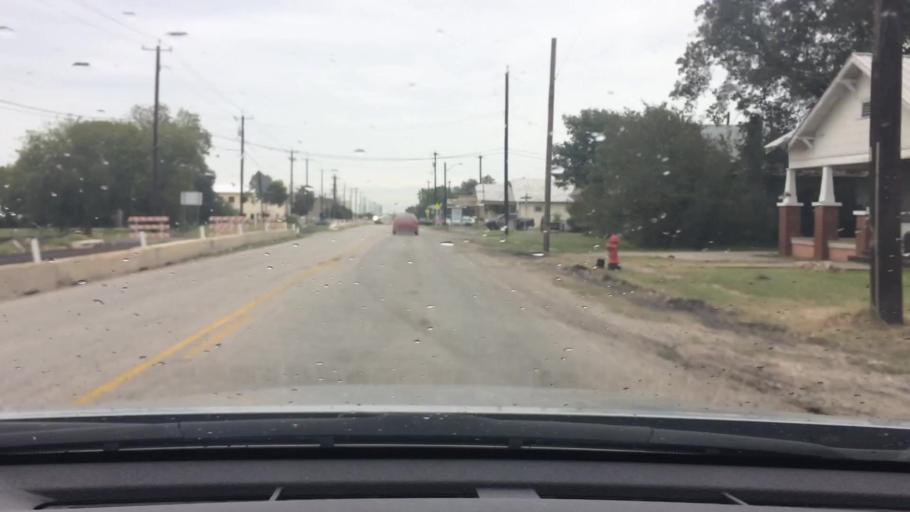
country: US
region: Texas
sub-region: Bexar County
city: Converse
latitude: 29.5167
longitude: -98.3131
